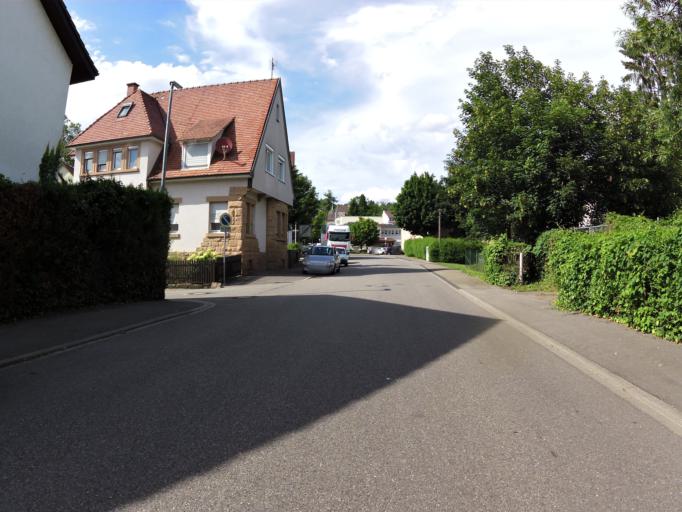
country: DE
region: Baden-Wuerttemberg
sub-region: Freiburg Region
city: Lahr
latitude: 48.3389
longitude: 7.8591
